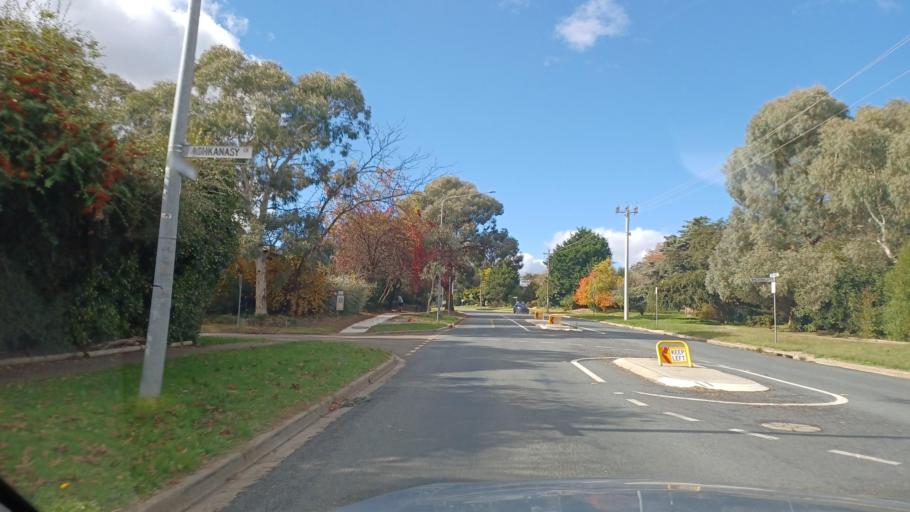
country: AU
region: Australian Capital Territory
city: Belconnen
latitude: -35.2076
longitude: 149.0659
